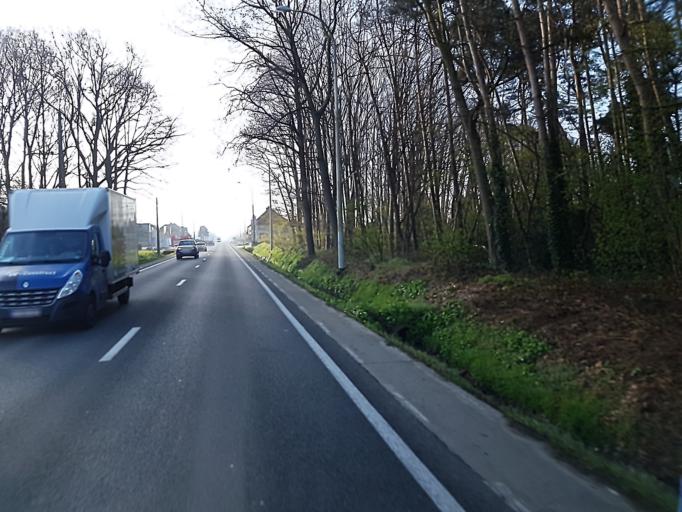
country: BE
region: Flanders
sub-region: Provincie Vlaams-Brabant
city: Begijnendijk
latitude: 51.0246
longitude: 4.7853
